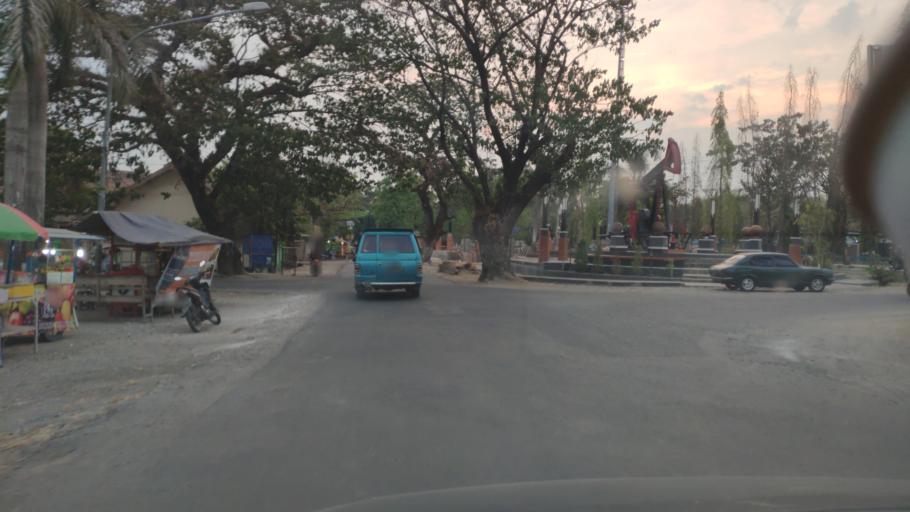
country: ID
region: Central Java
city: Cepu
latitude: -7.1497
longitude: 111.5892
